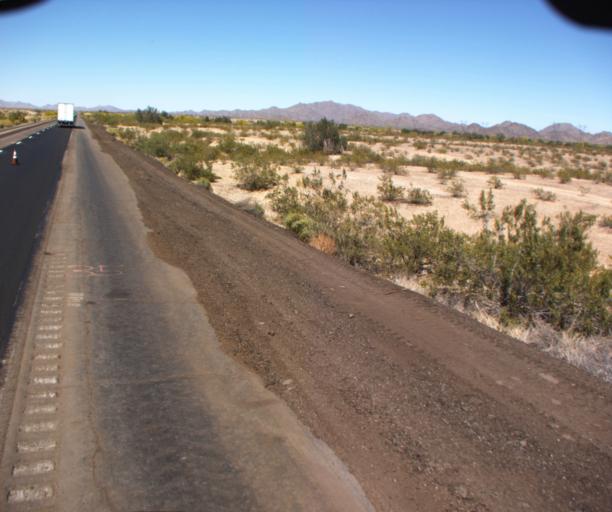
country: US
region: Arizona
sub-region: Maricopa County
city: Gila Bend
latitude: 33.0546
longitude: -112.6438
